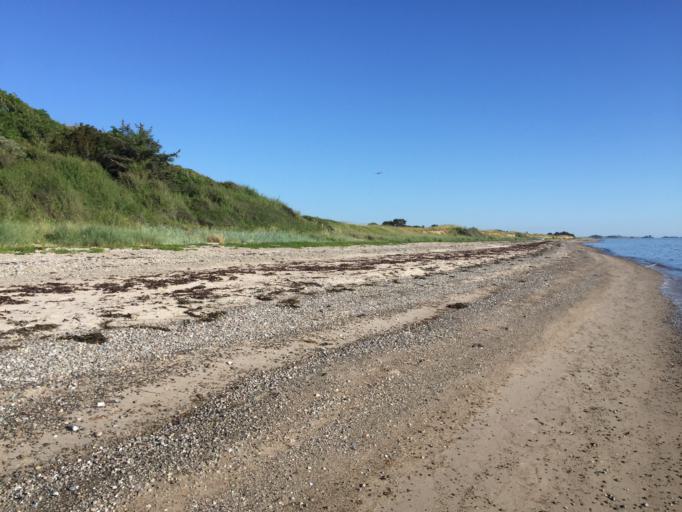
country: DK
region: Zealand
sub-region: Slagelse Kommune
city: Korsor
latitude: 55.2233
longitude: 11.1719
